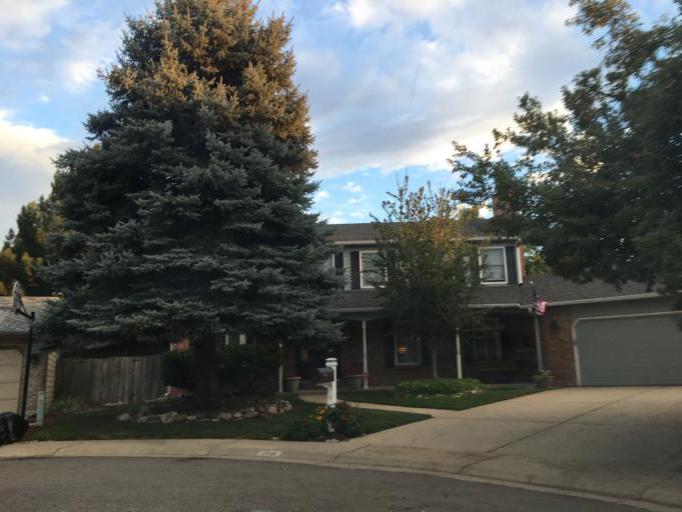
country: US
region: Colorado
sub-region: Adams County
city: Aurora
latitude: 39.6797
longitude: -104.8573
